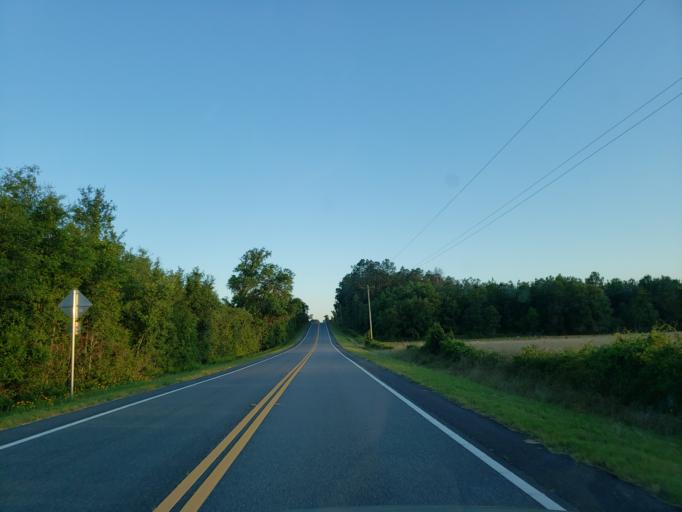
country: US
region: Florida
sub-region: Madison County
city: Madison
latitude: 30.5893
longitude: -83.2414
